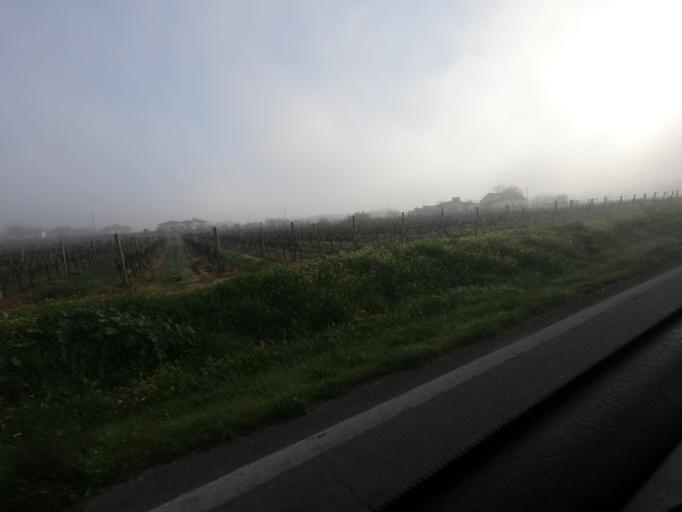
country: PT
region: Setubal
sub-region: Palmela
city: Pinhal Novo
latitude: 38.6063
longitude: -8.9070
